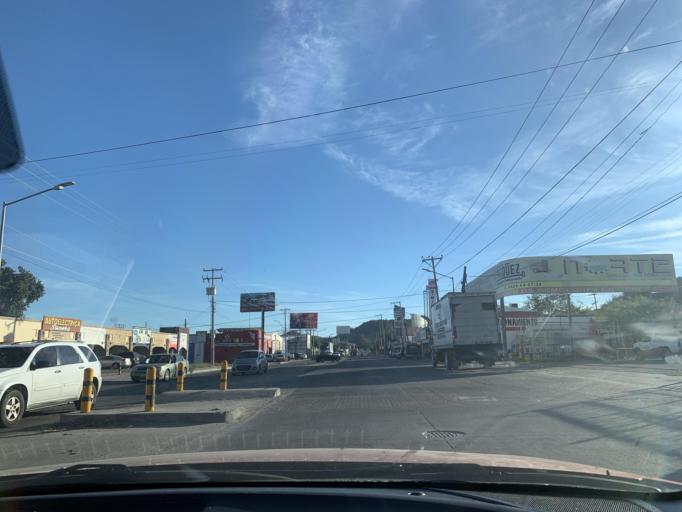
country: MX
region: Sonora
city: Hermosillo
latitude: 29.0955
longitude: -110.9311
